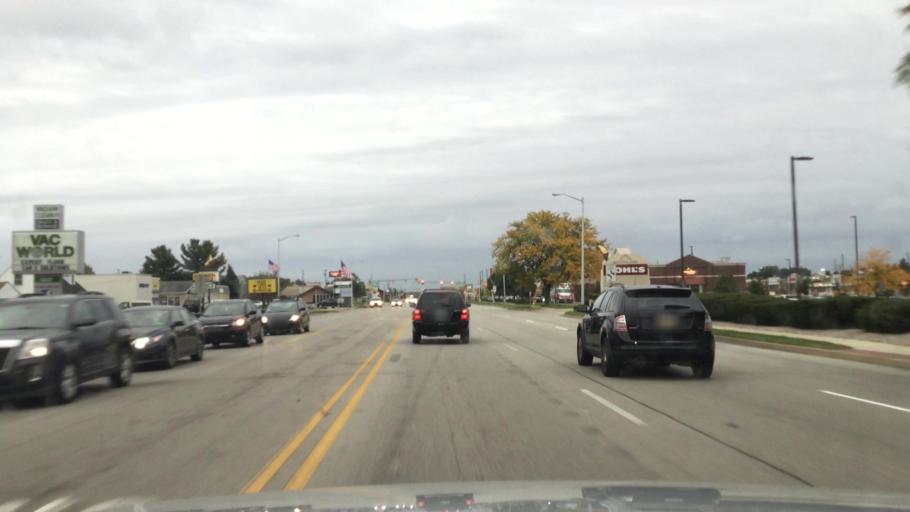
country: US
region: Michigan
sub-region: Kalamazoo County
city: Portage
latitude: 42.2298
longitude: -85.5892
